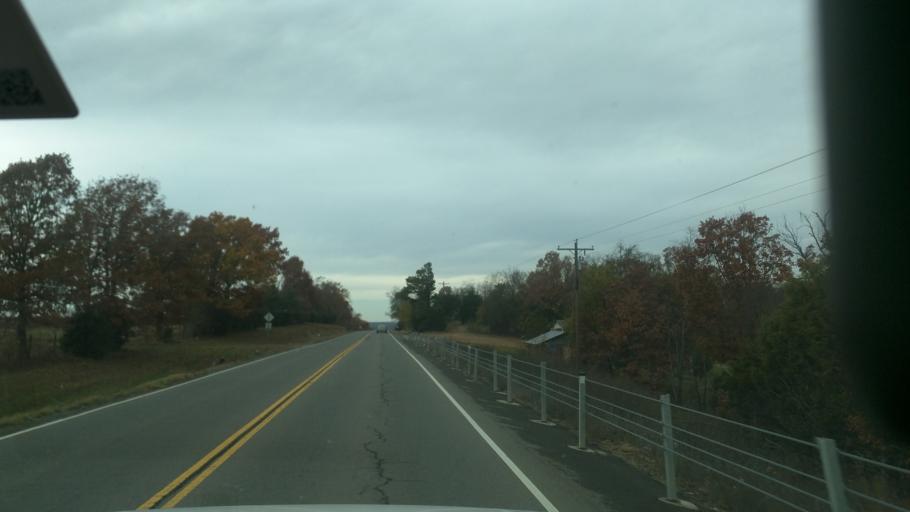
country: US
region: Oklahoma
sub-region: Cherokee County
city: Park Hill
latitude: 35.8998
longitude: -94.8044
